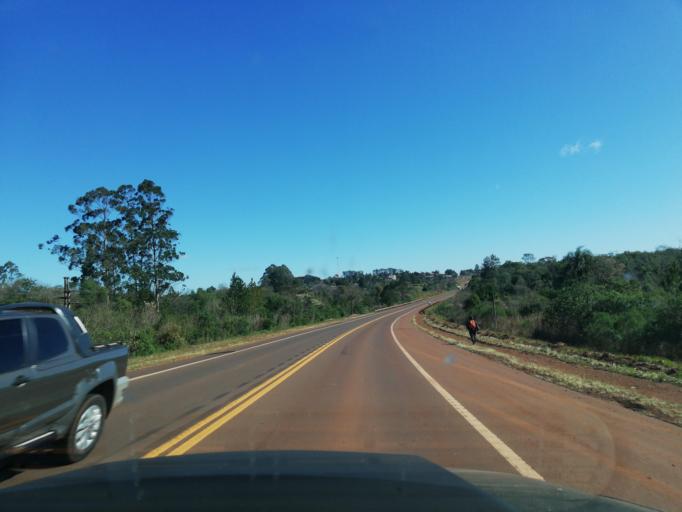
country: AR
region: Misiones
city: Aristobulo del Valle
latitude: -27.0980
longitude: -54.8752
